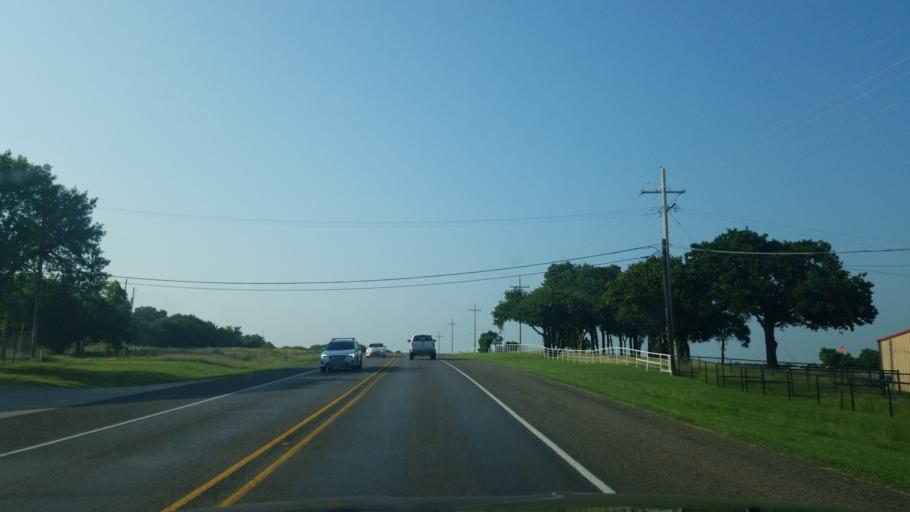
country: US
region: Texas
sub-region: Denton County
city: Aubrey
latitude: 33.3287
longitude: -96.9705
